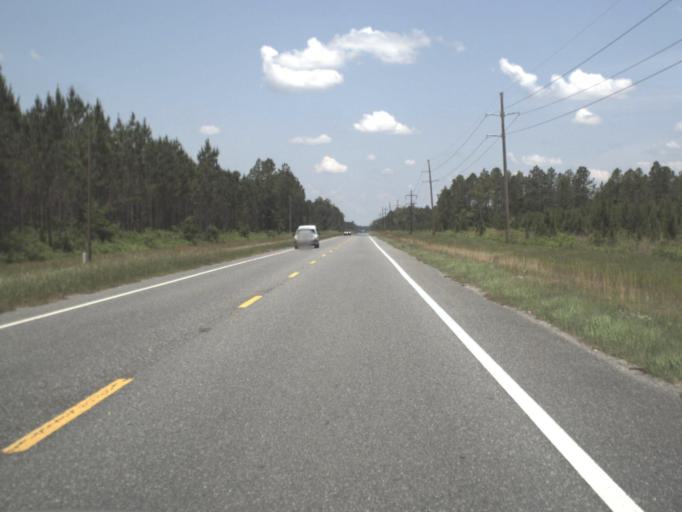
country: US
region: Florida
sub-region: Bradford County
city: Starke
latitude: 29.9726
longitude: -82.2142
